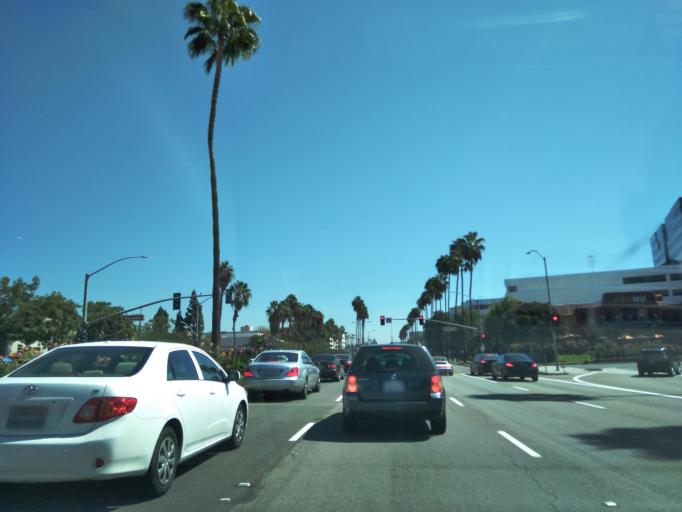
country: US
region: California
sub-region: Orange County
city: Irvine
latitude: 33.6852
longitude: -117.8536
